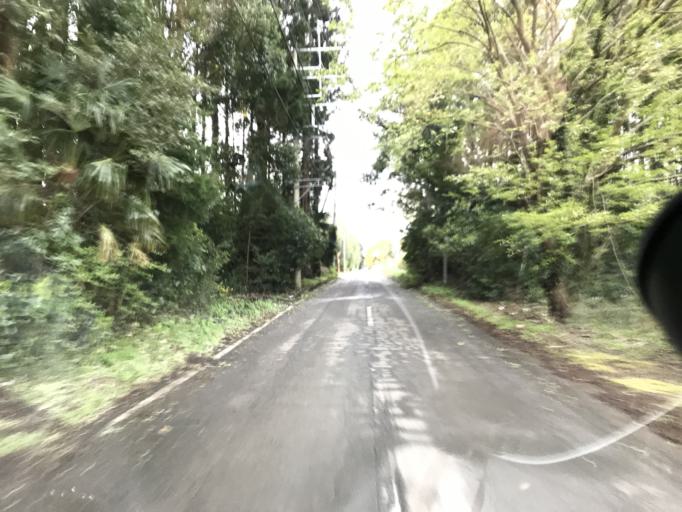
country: JP
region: Chiba
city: Sawara
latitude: 35.7954
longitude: 140.4498
